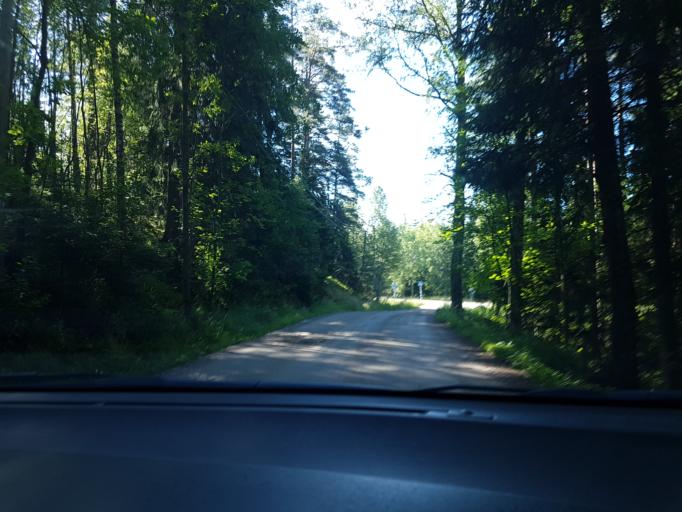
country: FI
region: Uusimaa
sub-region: Helsinki
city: Sibbo
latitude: 60.2621
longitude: 25.2270
